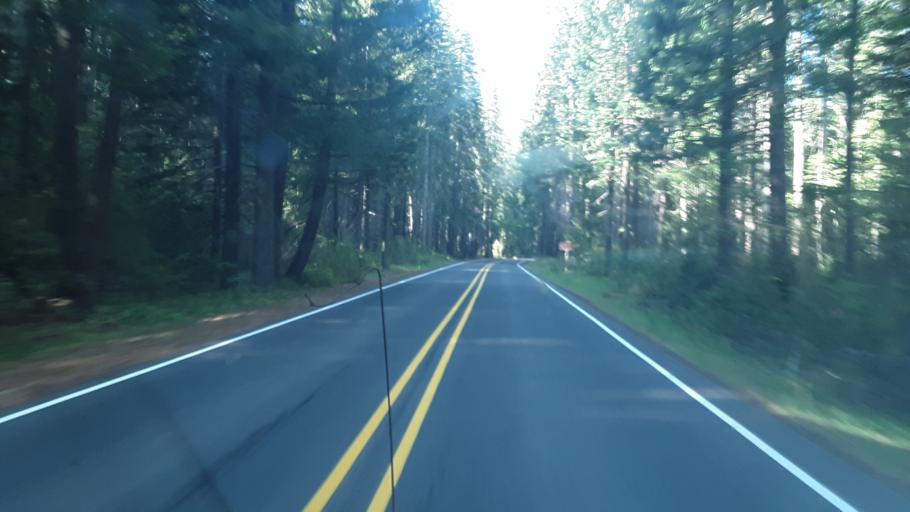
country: US
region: Oregon
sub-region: Jackson County
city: Shady Cove
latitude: 42.9302
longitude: -122.4226
